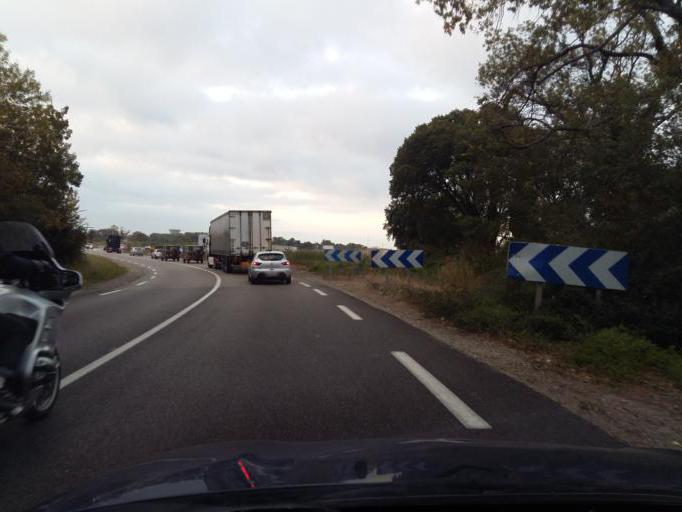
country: FR
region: Provence-Alpes-Cote d'Azur
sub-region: Departement des Bouches-du-Rhone
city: Miramas
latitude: 43.6095
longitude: 5.0103
